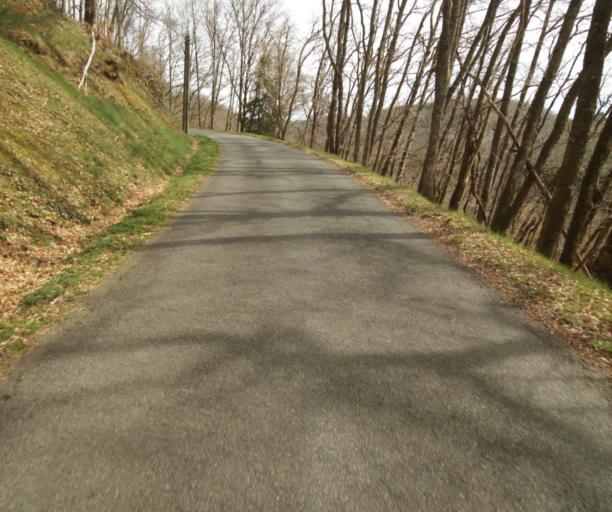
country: FR
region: Limousin
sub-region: Departement de la Correze
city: Naves
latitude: 45.3503
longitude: 1.8158
